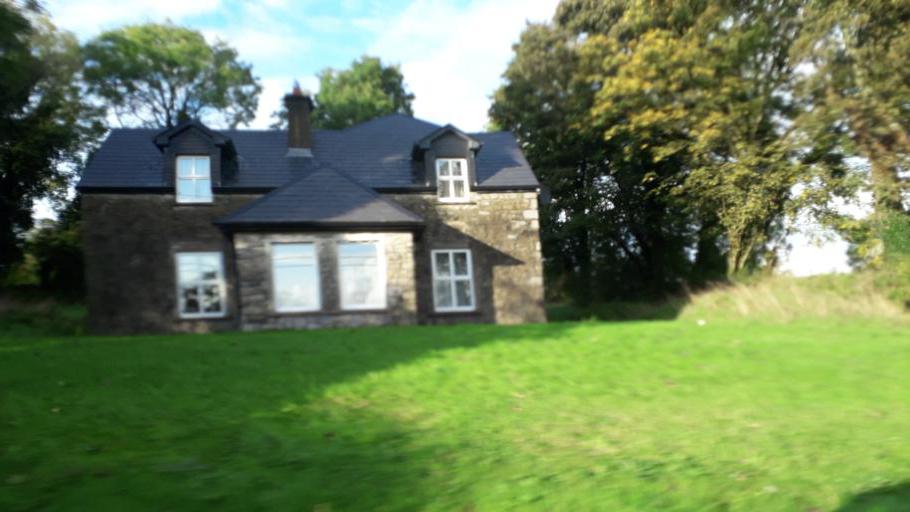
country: IE
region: Connaught
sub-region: Roscommon
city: Roscommon
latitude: 53.7726
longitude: -8.2292
